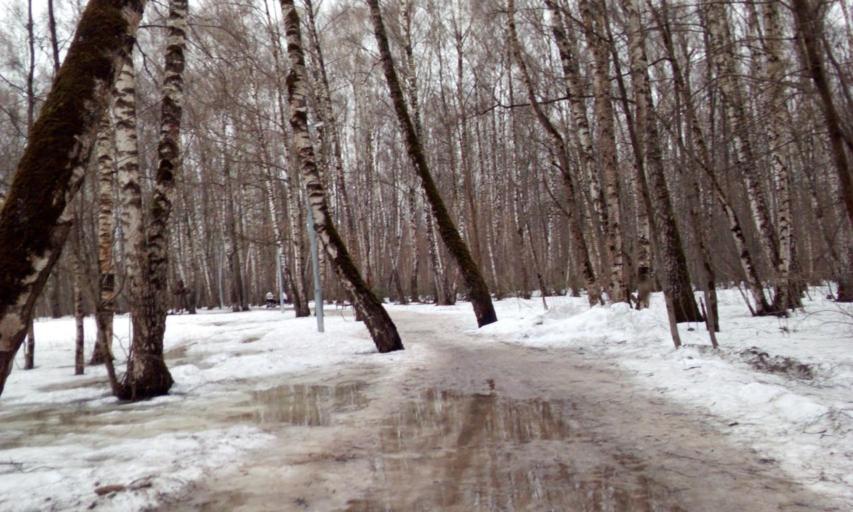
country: RU
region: Moscow
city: Troparevo
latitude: 55.6380
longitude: 37.4814
